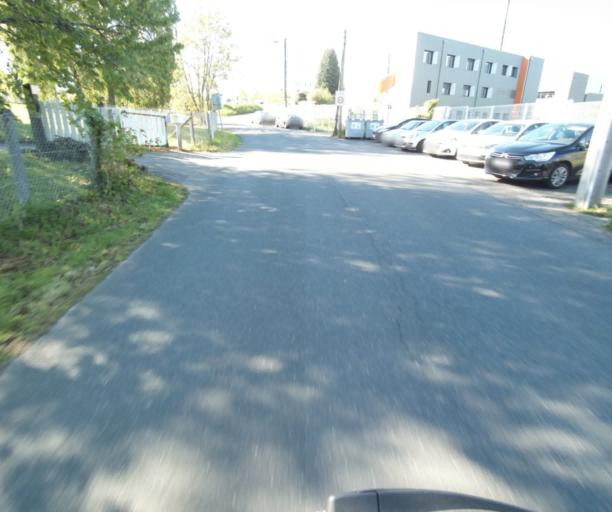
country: FR
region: Limousin
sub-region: Departement de la Correze
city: Tulle
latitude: 45.2704
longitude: 1.7845
